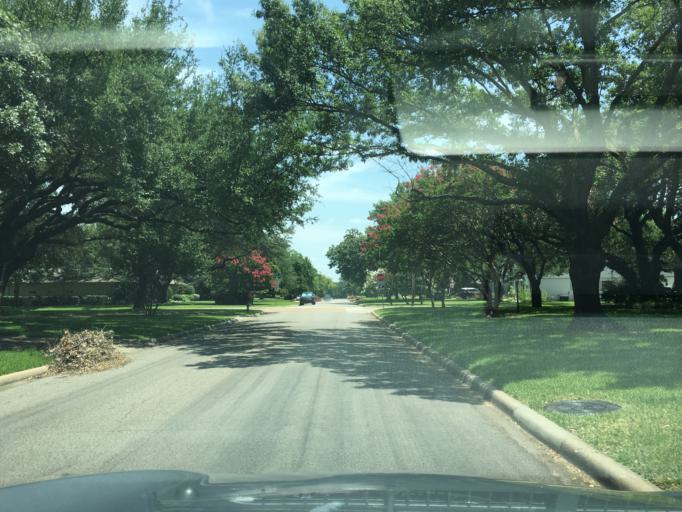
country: US
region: Texas
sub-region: Dallas County
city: Addison
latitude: 32.9142
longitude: -96.8093
